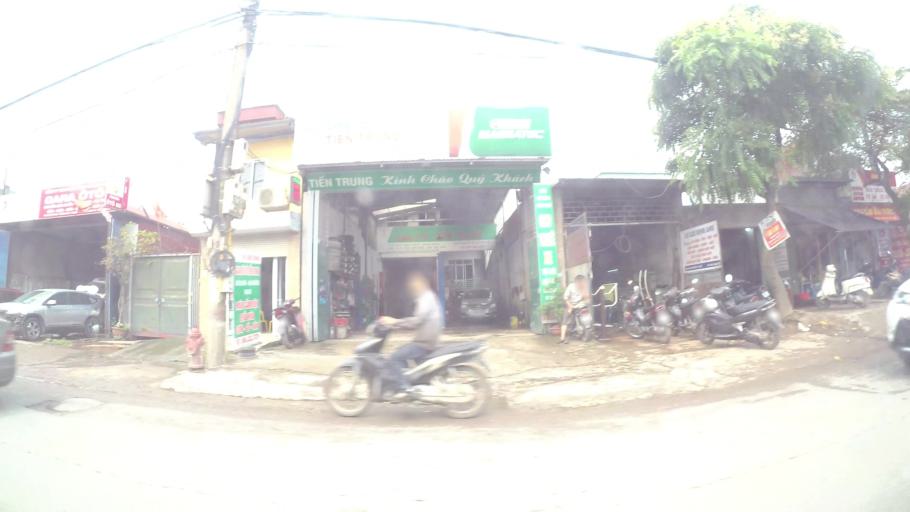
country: VN
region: Ha Noi
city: Van Dien
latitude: 20.9727
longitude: 105.8663
